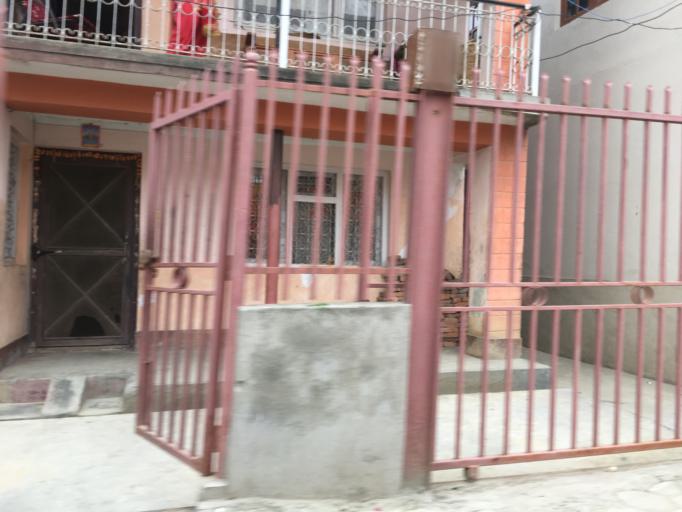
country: NP
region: Central Region
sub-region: Bagmati Zone
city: Kathmandu
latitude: 27.7395
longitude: 85.3490
